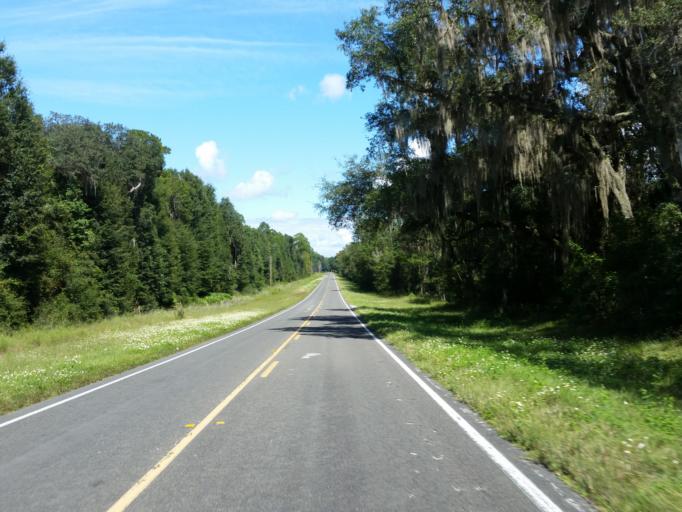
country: US
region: Florida
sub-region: Alachua County
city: Gainesville
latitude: 29.5889
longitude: -82.2354
